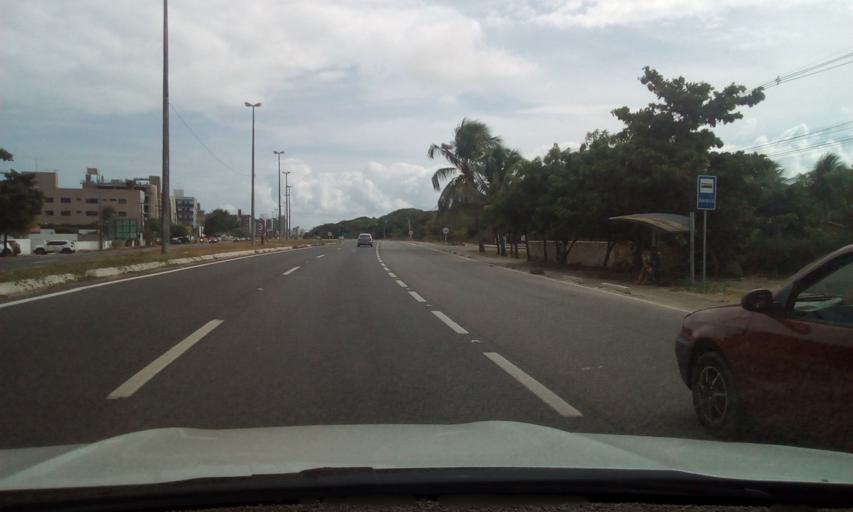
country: BR
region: Paraiba
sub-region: Cabedelo
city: Cabedelo
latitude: -6.9892
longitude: -34.8286
